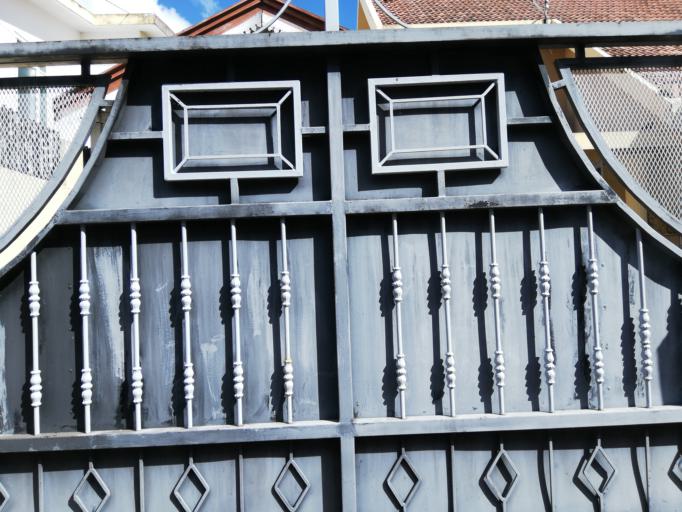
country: MU
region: Moka
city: Moka
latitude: -20.2254
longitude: 57.4760
